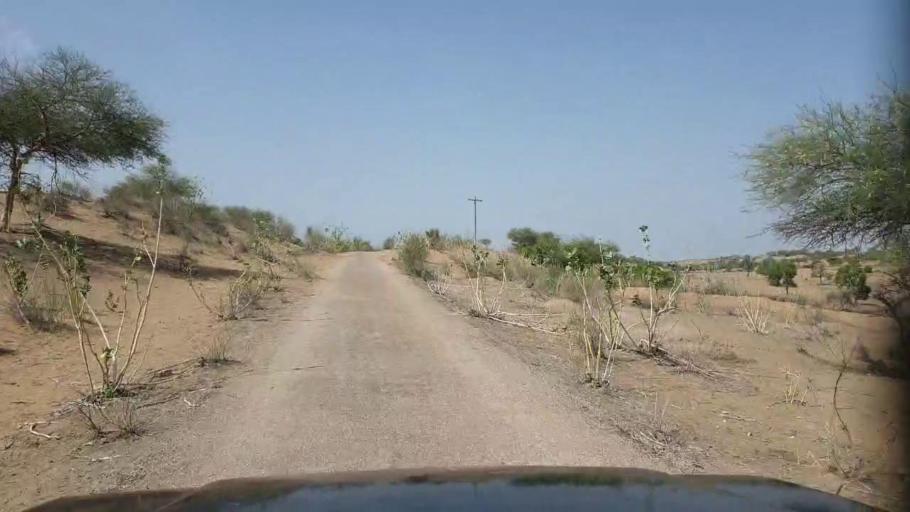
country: PK
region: Sindh
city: Mithi
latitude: 24.9680
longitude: 69.9687
